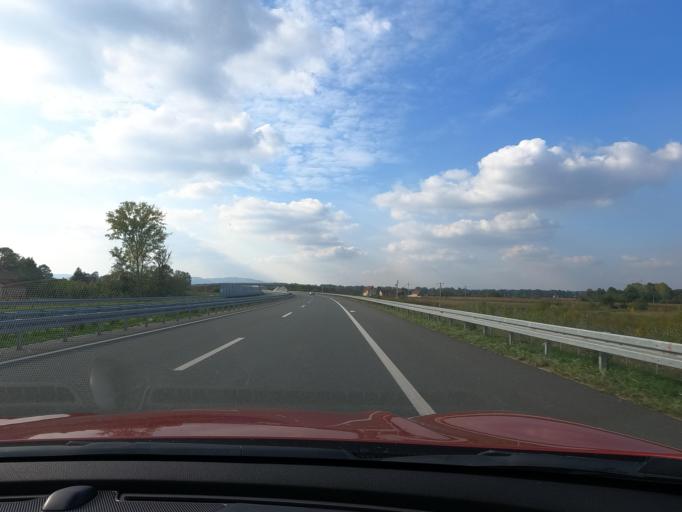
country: RS
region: Central Serbia
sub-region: Kolubarski Okrug
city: Lajkovac
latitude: 44.3457
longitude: 20.1814
